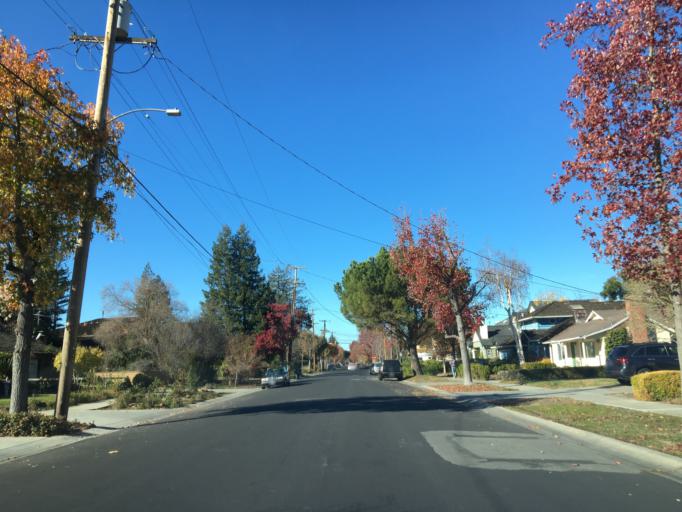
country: US
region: California
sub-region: Santa Clara County
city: Palo Alto
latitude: 37.4283
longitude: -122.1305
